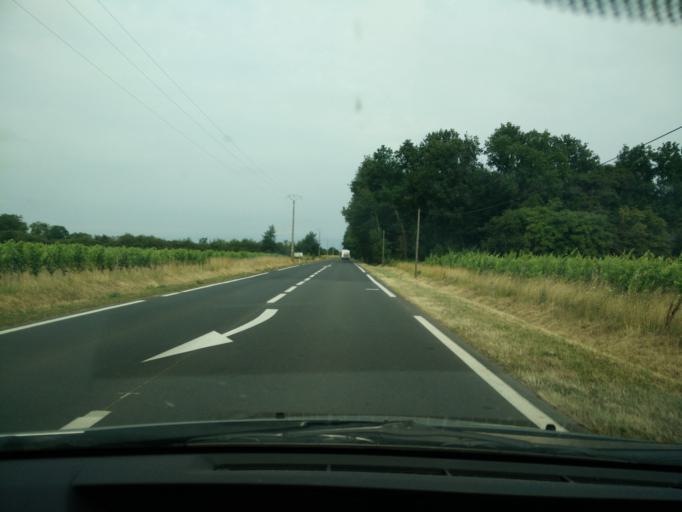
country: FR
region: Pays de la Loire
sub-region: Departement de Maine-et-Loire
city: Vaudelnay
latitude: 47.1698
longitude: -0.2174
